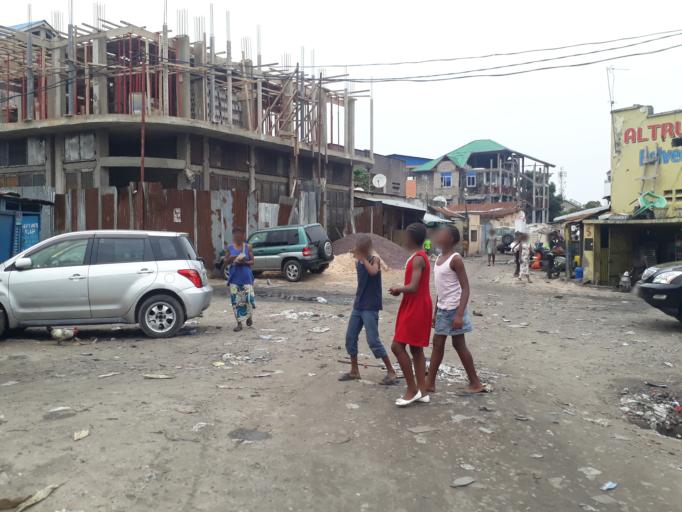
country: CD
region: Kinshasa
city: Kinshasa
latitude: -4.3092
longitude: 15.3190
